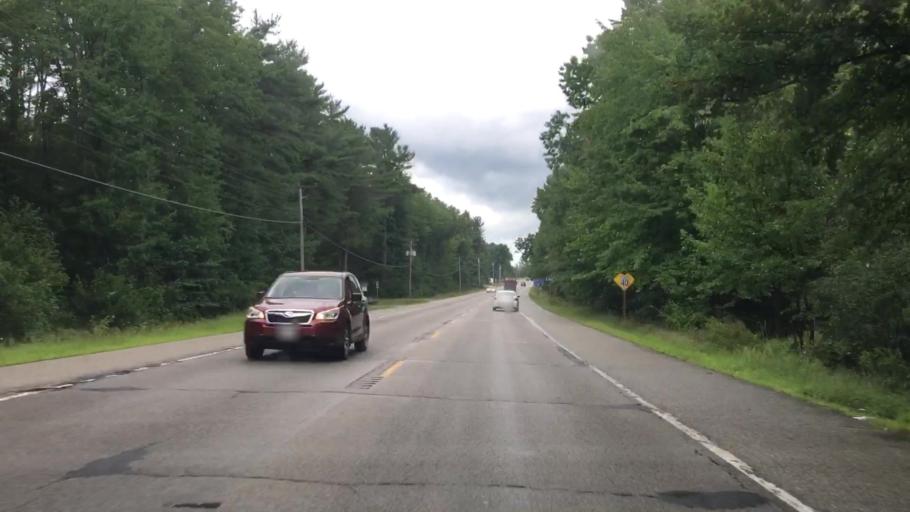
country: US
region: Maine
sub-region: York County
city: South Sanford
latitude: 43.4043
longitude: -70.7411
